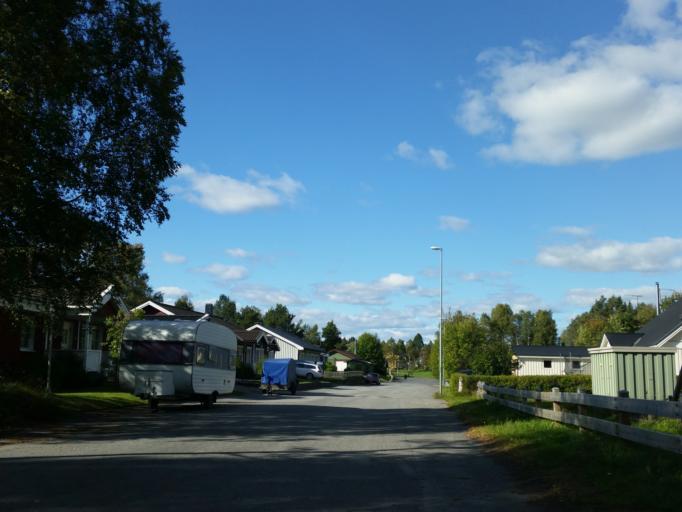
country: SE
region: Vaesterbotten
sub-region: Robertsfors Kommun
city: Robertsfors
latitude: 64.0559
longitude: 20.8577
